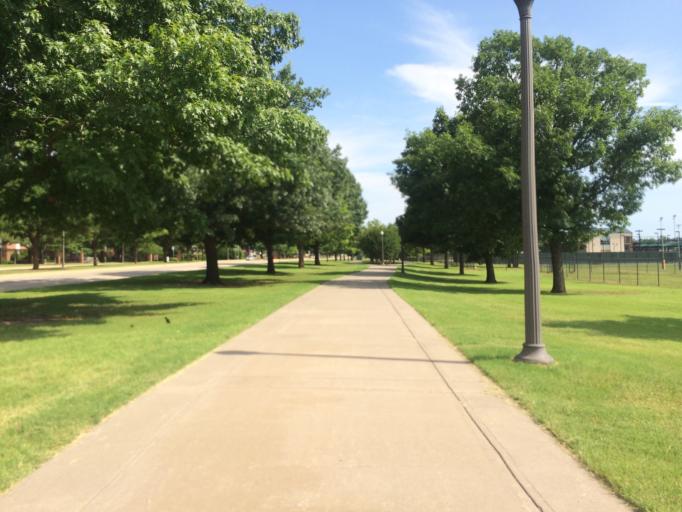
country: US
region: Oklahoma
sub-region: Cleveland County
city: Norman
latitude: 35.1855
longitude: -97.4498
